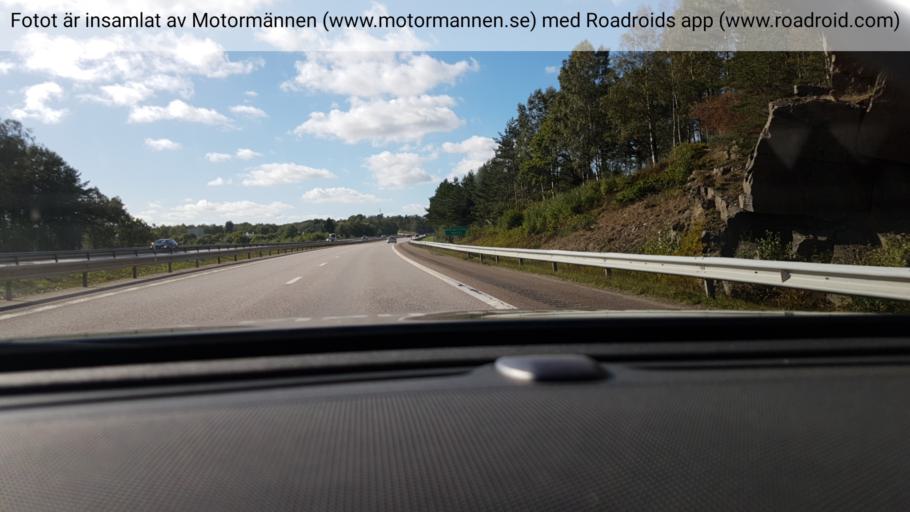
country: SE
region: Vaestra Goetaland
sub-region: Harryda Kommun
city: Molnlycke
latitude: 57.6712
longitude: 12.1046
